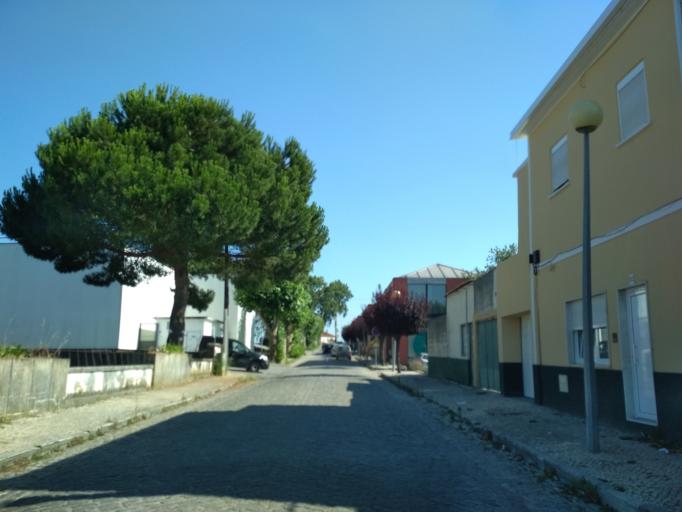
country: PT
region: Aveiro
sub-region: Mealhada
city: Mealhada
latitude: 40.3719
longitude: -8.4533
